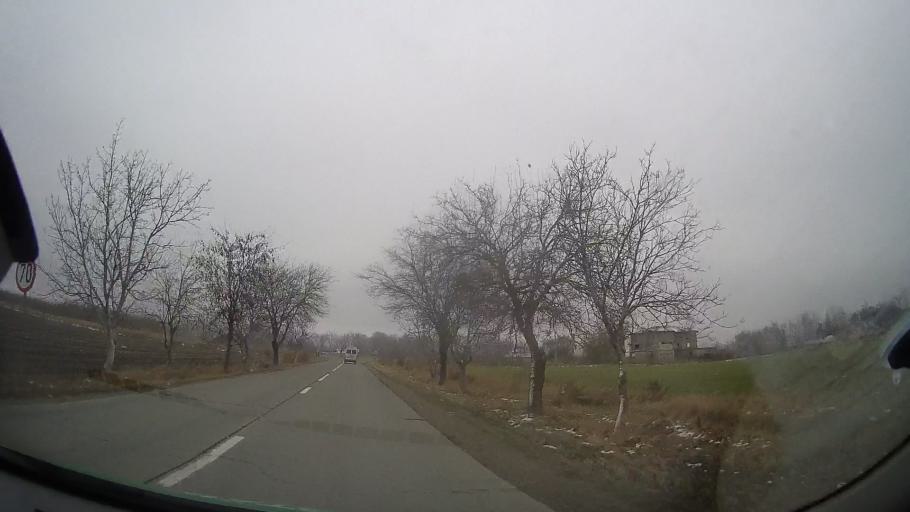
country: RO
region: Vaslui
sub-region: Municipiul Barlad
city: Barlad
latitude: 46.1978
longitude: 27.6408
